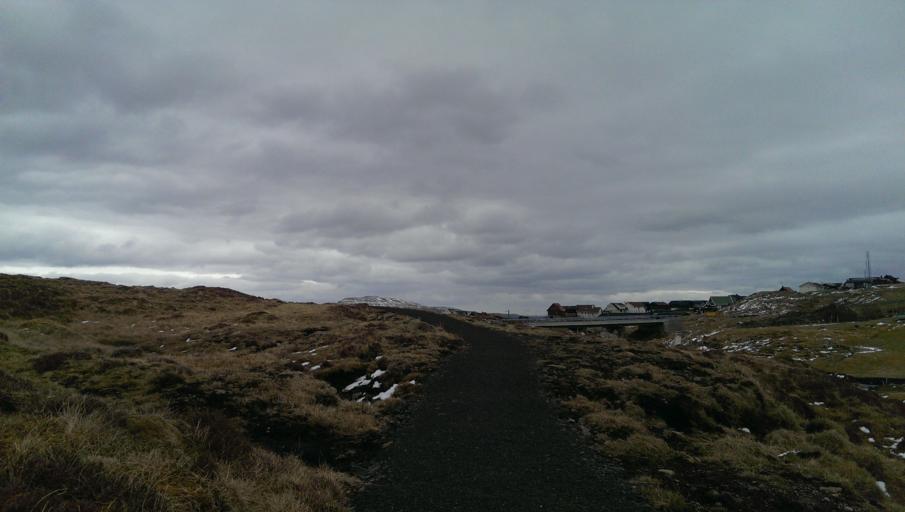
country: FO
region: Streymoy
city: Hoyvik
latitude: 62.0330
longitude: -6.7989
